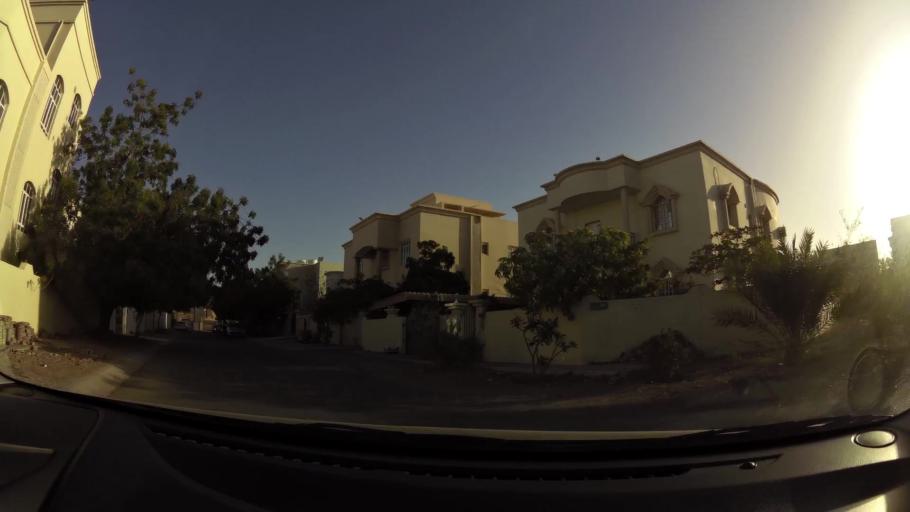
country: OM
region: Muhafazat Masqat
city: As Sib al Jadidah
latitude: 23.6113
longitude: 58.2308
